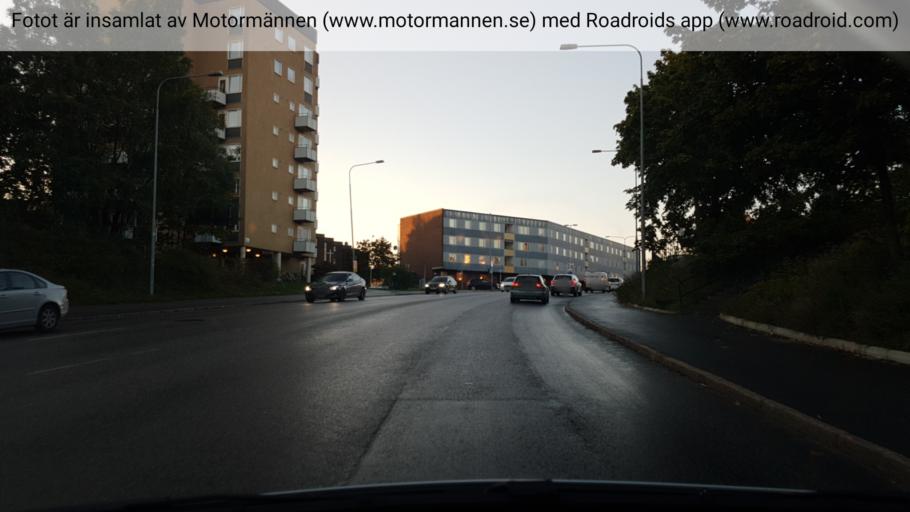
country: SE
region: Stockholm
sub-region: Sodertalje Kommun
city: Soedertaelje
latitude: 59.2013
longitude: 17.6328
